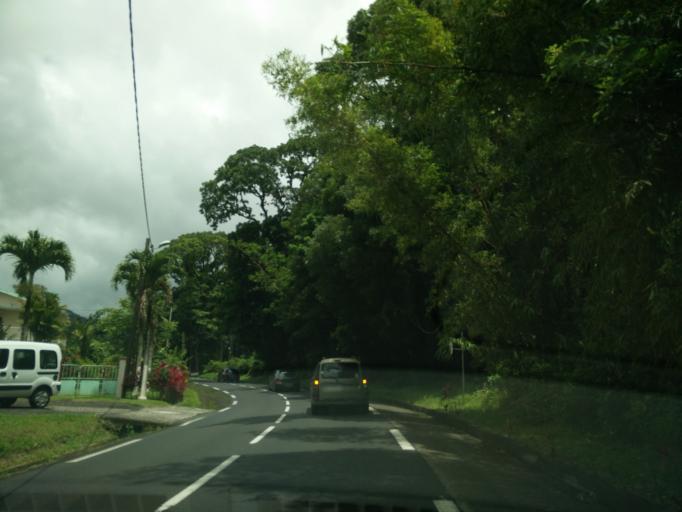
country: MQ
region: Martinique
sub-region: Martinique
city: Le Morne-Rouge
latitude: 14.7636
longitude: -61.1194
